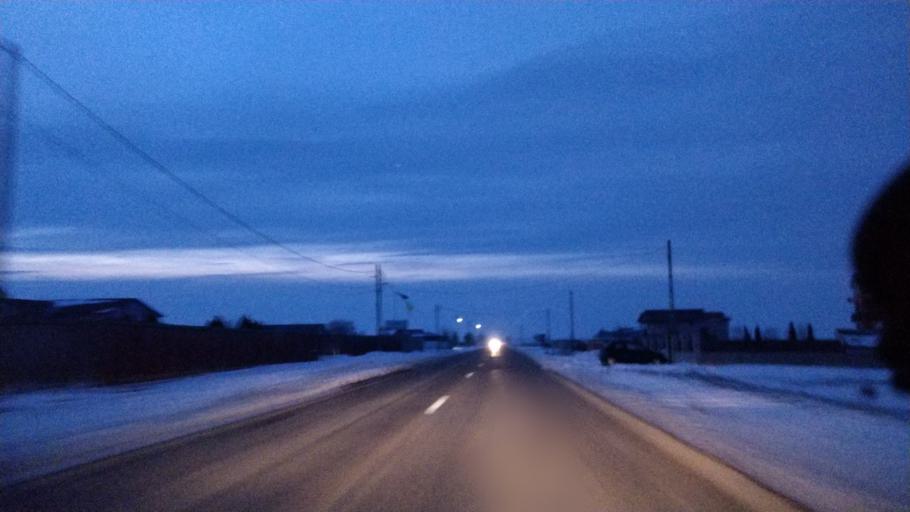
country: RO
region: Vrancea
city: Vulturu de Sus
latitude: 45.6386
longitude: 27.3709
